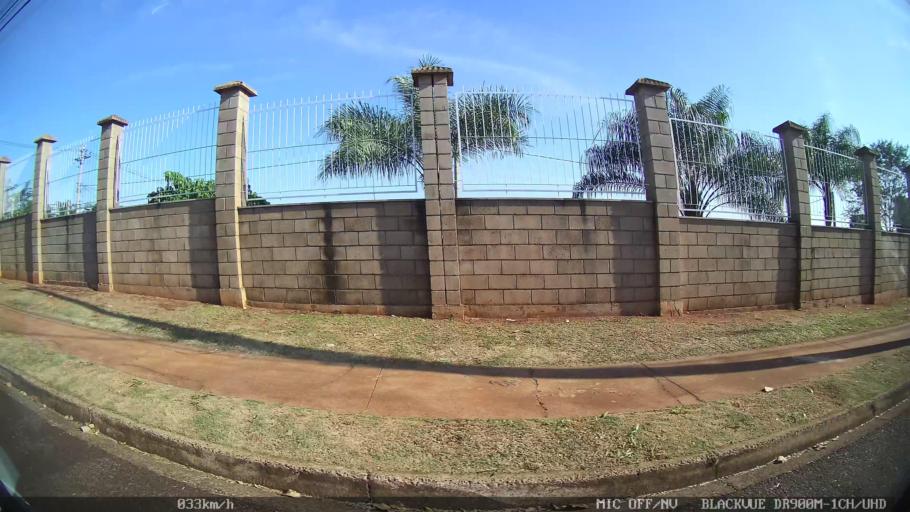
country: BR
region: Sao Paulo
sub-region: Sao Jose Do Rio Preto
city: Sao Jose do Rio Preto
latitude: -20.7701
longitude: -49.3309
